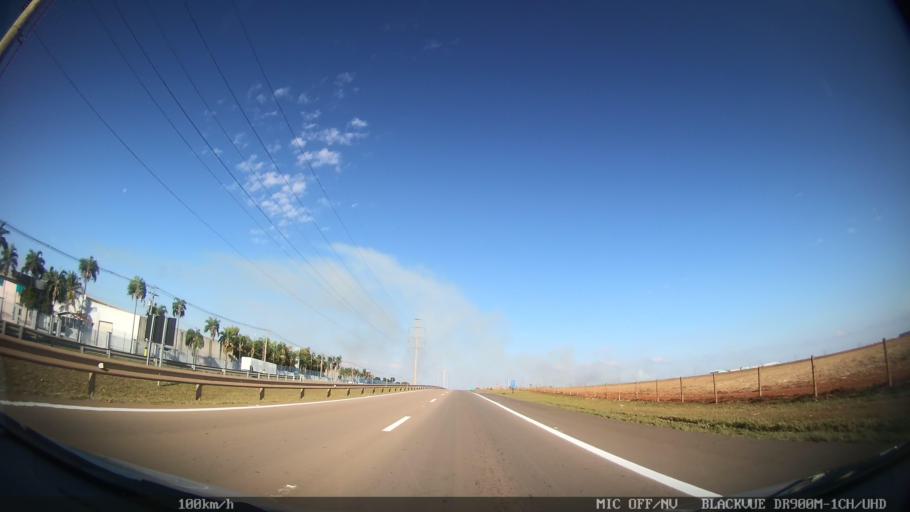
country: BR
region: Sao Paulo
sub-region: Piracicaba
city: Piracicaba
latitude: -22.6682
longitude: -47.6047
